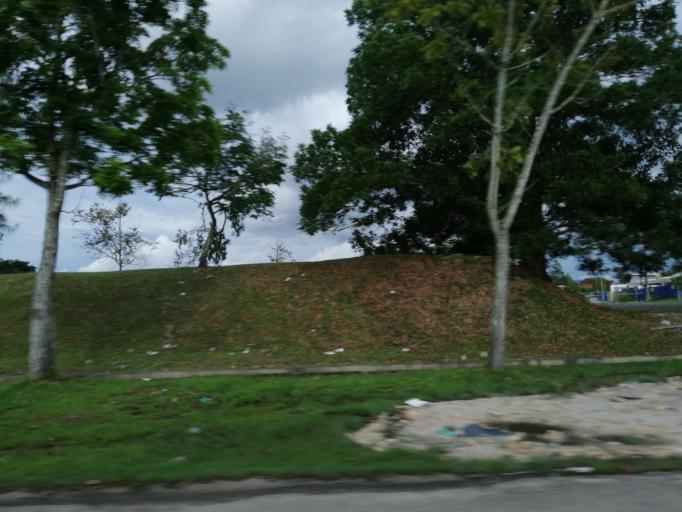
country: MY
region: Penang
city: Tasek Glugor
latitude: 5.5013
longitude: 100.6242
